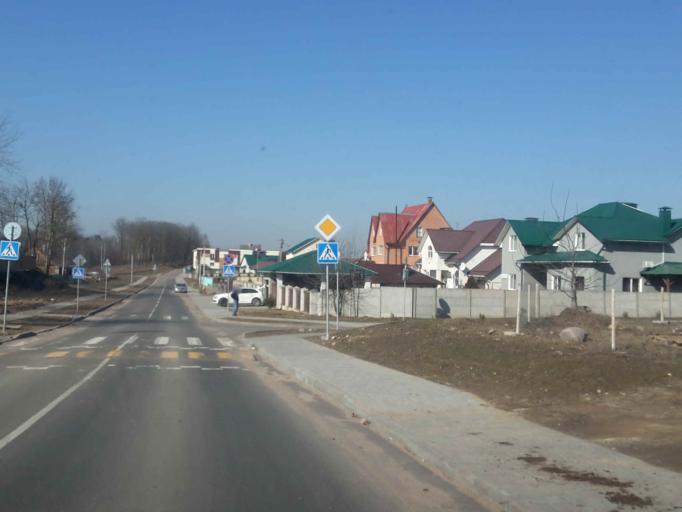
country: BY
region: Minsk
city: Zhdanovichy
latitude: 53.9203
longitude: 27.4062
